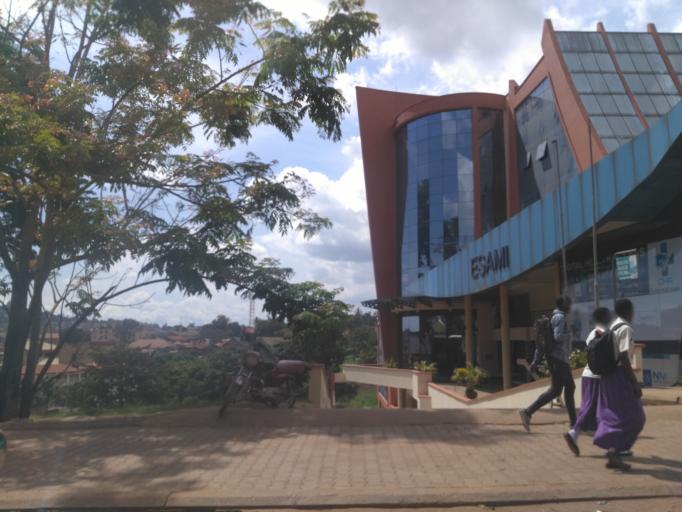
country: UG
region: Central Region
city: Kampala Central Division
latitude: 0.3267
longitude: 32.5742
